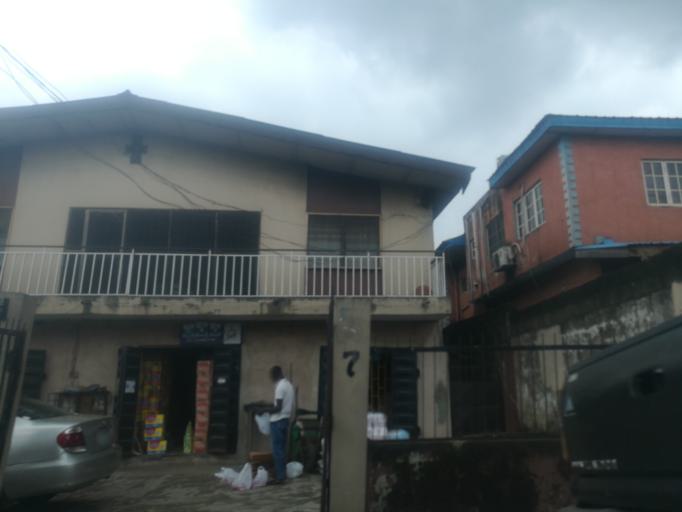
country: NG
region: Lagos
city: Ojota
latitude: 6.5972
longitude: 3.3873
